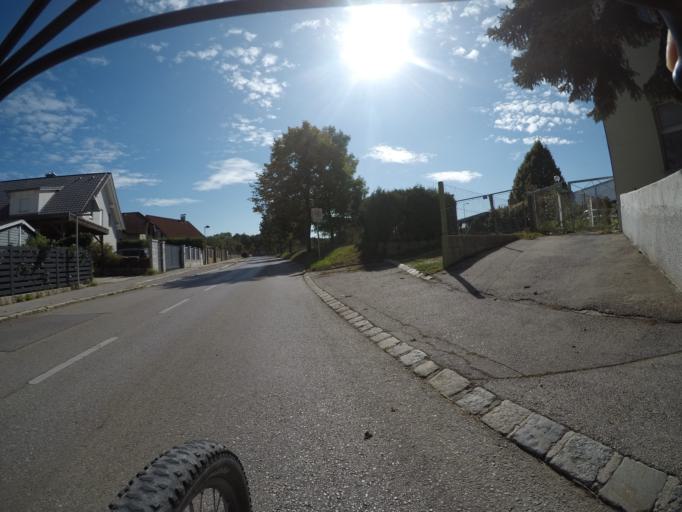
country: AT
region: Lower Austria
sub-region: Politischer Bezirk Modling
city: Maria Enzersdorf
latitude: 48.0972
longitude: 16.2945
